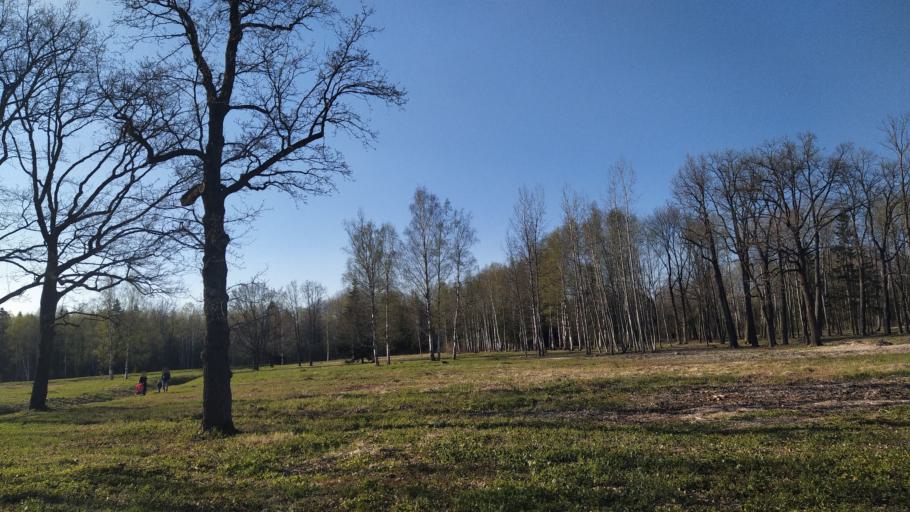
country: RU
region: St.-Petersburg
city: Pushkin
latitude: 59.7123
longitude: 30.3719
